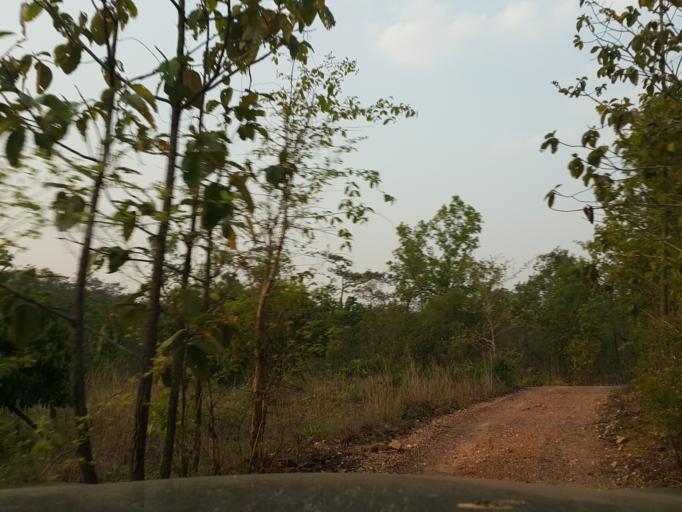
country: TH
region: Lamphun
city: Thung Hua Chang
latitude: 17.9043
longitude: 99.0811
